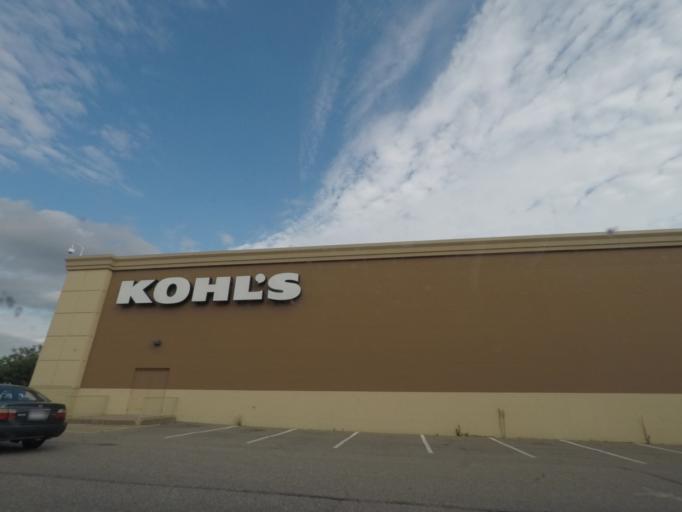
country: US
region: Massachusetts
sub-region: Hampden County
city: West Springfield
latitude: 42.1286
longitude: -72.6241
